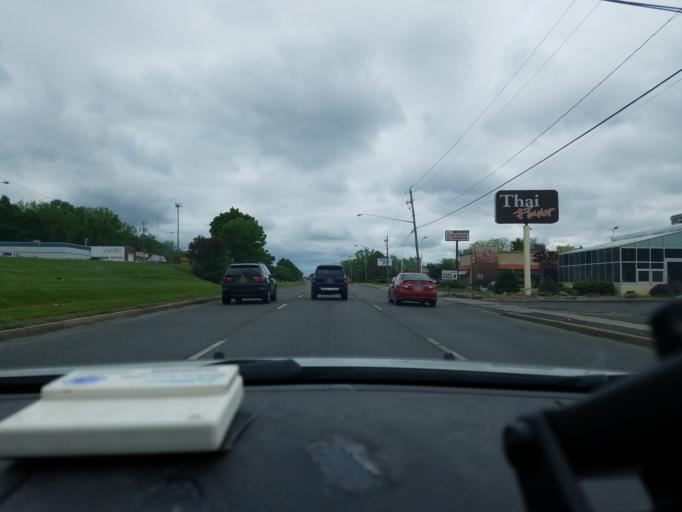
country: US
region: New York
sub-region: Onondaga County
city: East Syracuse
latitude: 43.0552
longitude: -76.0913
